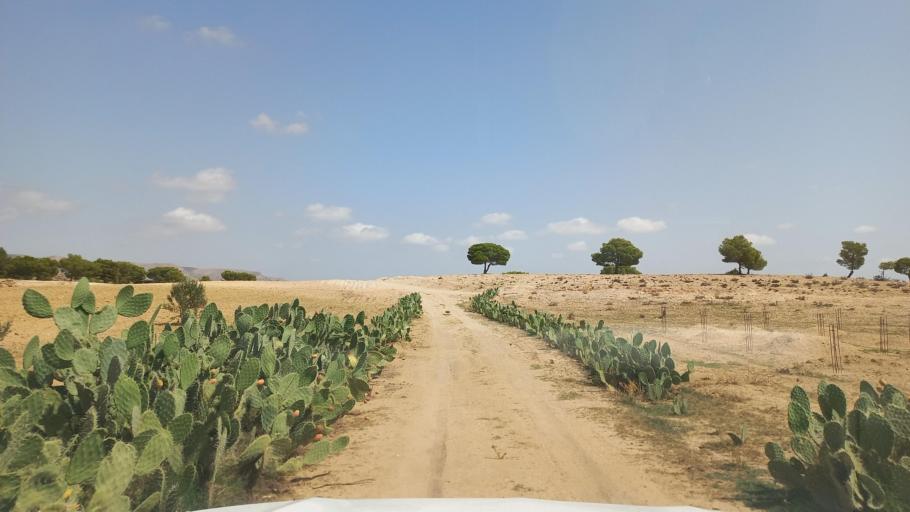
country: TN
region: Al Qasrayn
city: Sbiba
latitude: 35.3952
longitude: 8.9855
